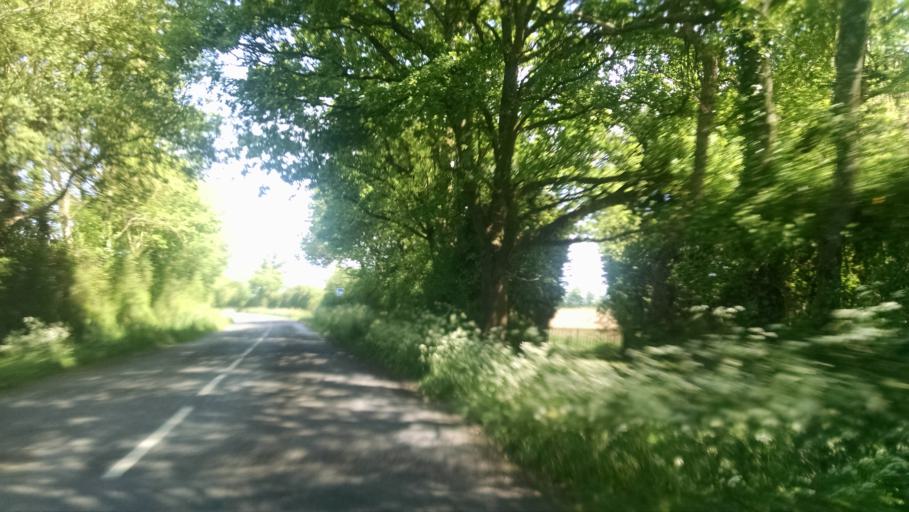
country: FR
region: Pays de la Loire
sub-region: Departement de la Loire-Atlantique
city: Saint-Hilaire-de-Clisson
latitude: 47.0373
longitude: -1.3244
